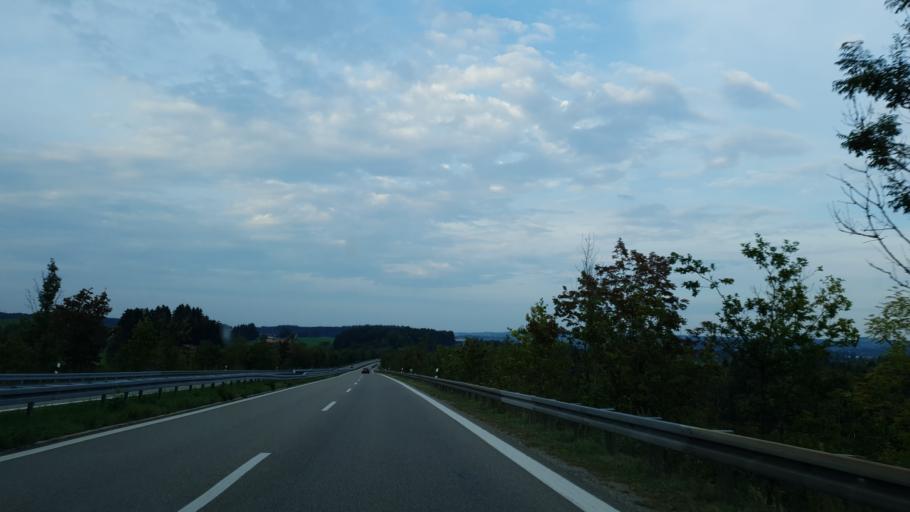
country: DE
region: Bavaria
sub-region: Swabia
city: Waltenhofen
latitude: 47.6730
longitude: 10.2766
